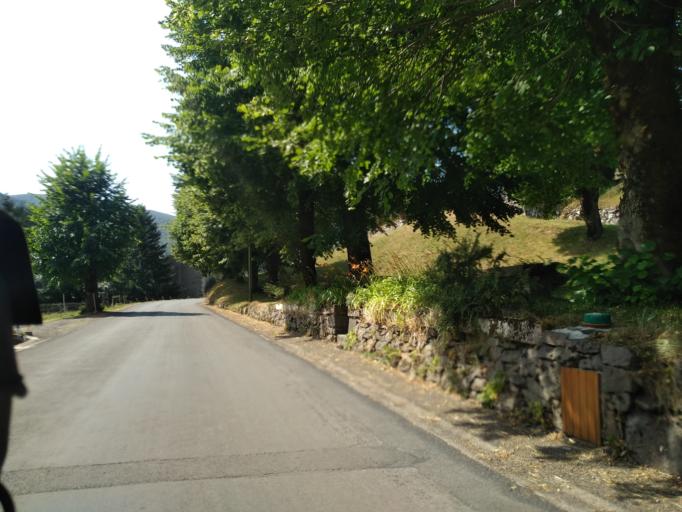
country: FR
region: Auvergne
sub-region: Departement du Cantal
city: Riom-es-Montagnes
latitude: 45.1615
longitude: 2.7070
